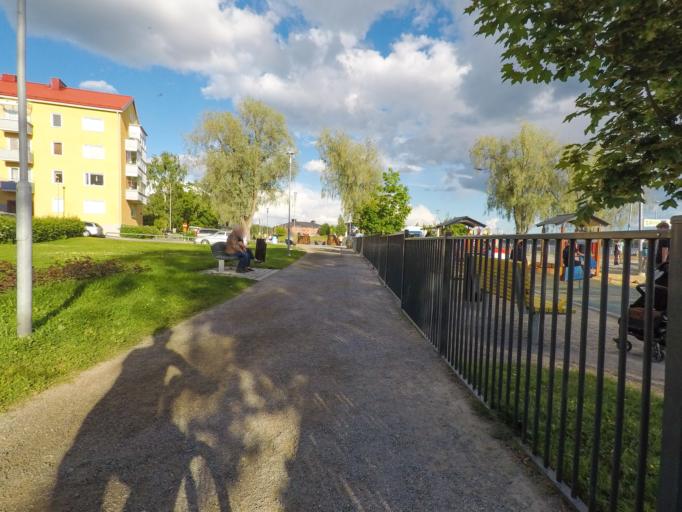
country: FI
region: Southern Savonia
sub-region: Savonlinna
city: Savonlinna
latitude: 61.8647
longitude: 28.8906
